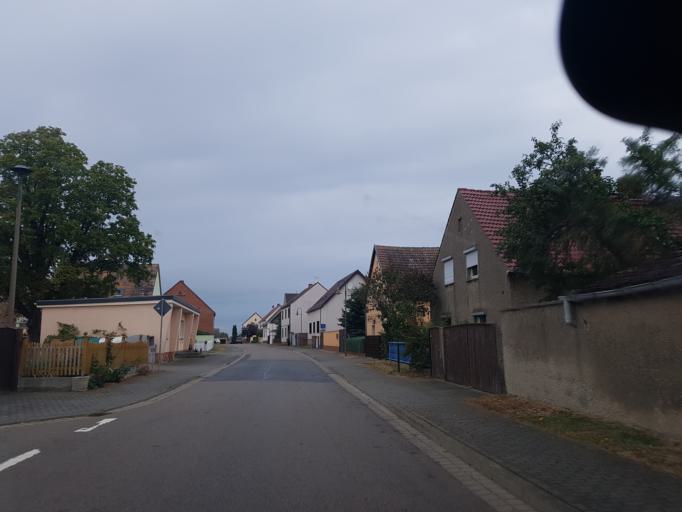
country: DE
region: Saxony-Anhalt
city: Elster
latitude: 51.7982
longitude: 12.8686
